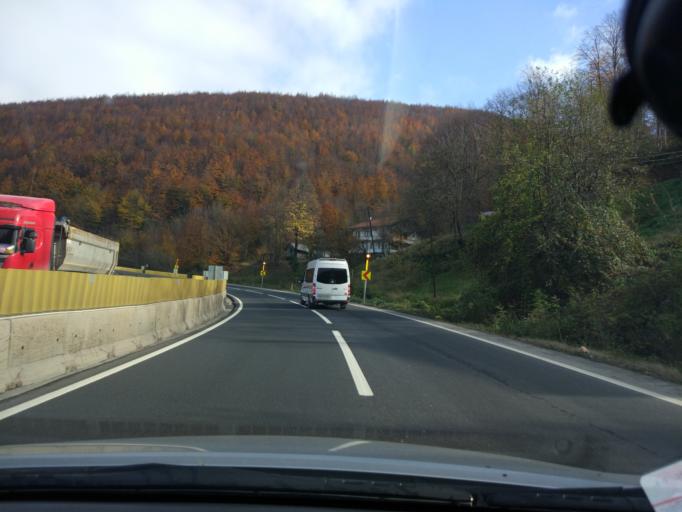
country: TR
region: Duzce
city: Kaynasli
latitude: 40.7537
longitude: 31.3638
